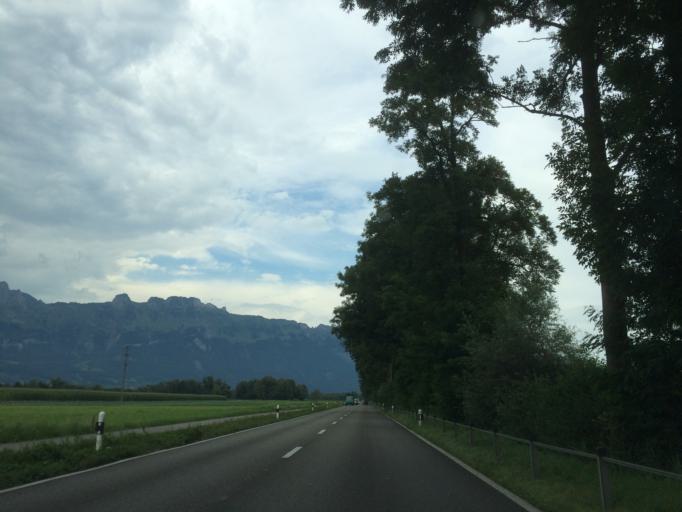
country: LI
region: Schaan
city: Schaan
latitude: 47.1842
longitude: 9.5061
